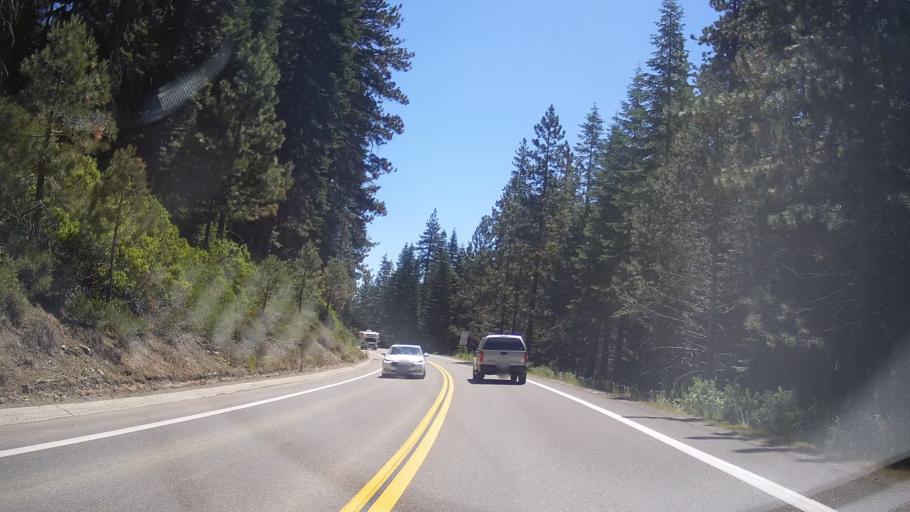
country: US
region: California
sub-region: Placer County
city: Sunnyside-Tahoe City
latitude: 39.1634
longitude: -120.1671
